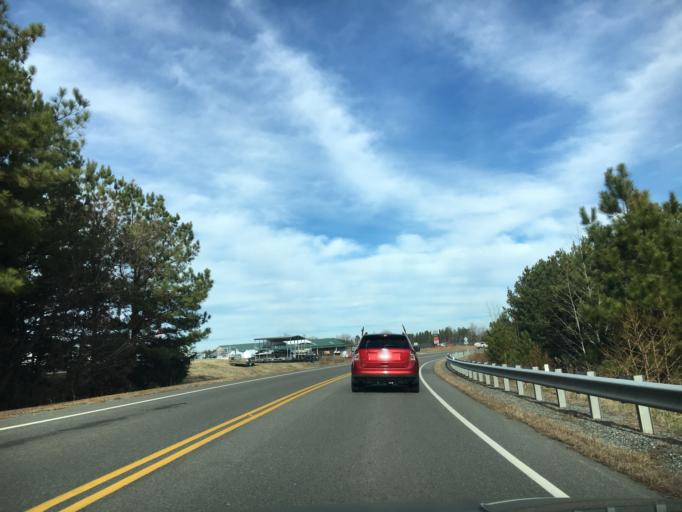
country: US
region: Virginia
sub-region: Louisa County
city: Louisa
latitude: 38.0739
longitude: -77.8820
